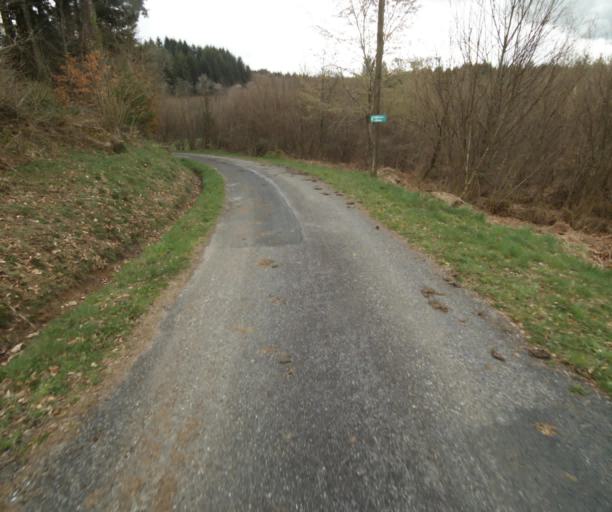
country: FR
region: Limousin
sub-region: Departement de la Correze
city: Correze
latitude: 45.2663
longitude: 1.9573
